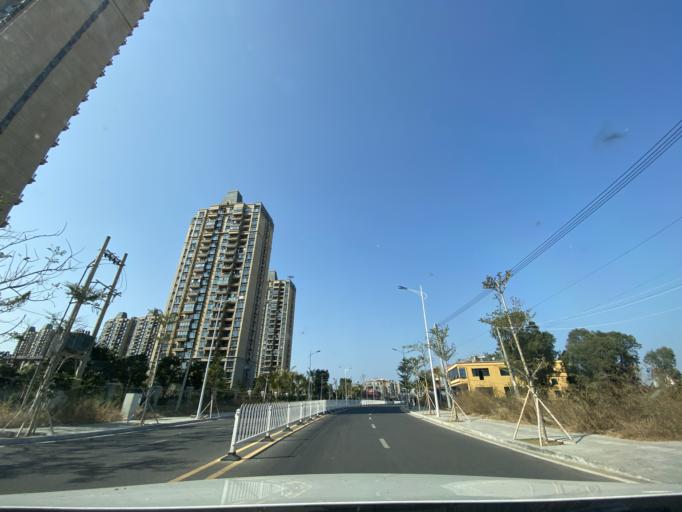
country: CN
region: Hainan
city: Yingzhou
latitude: 18.4153
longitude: 109.8538
